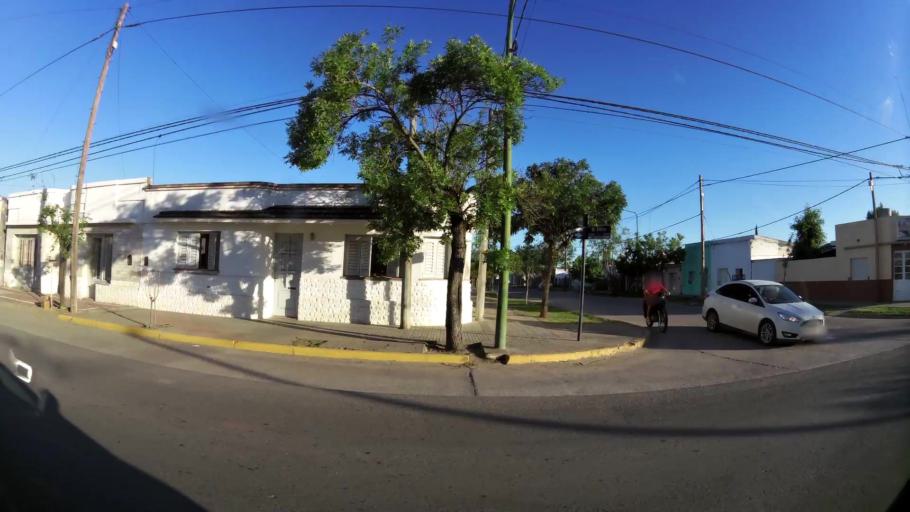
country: AR
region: Cordoba
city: Las Varillas
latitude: -31.8767
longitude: -62.7187
